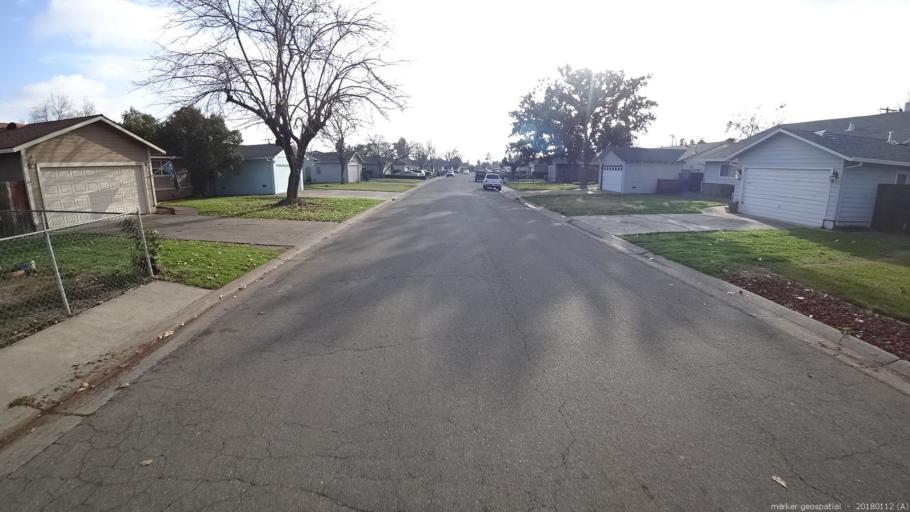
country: US
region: California
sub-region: Sacramento County
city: Rancho Cordova
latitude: 38.5990
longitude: -121.2931
